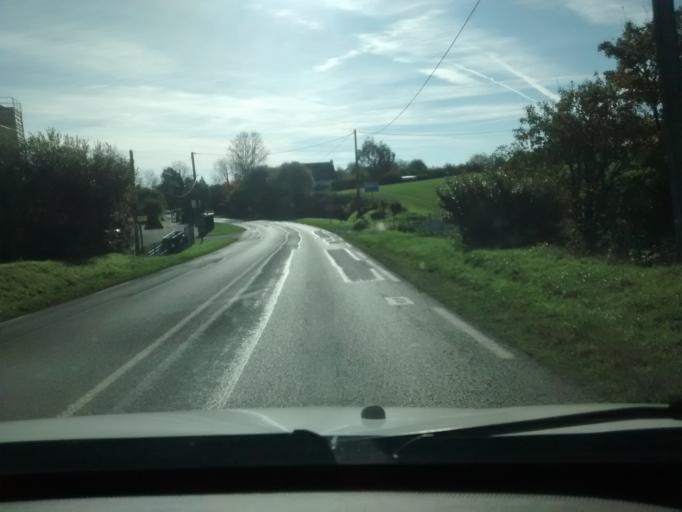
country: FR
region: Brittany
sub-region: Departement des Cotes-d'Armor
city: Langoat
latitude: 48.7630
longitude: -3.2967
